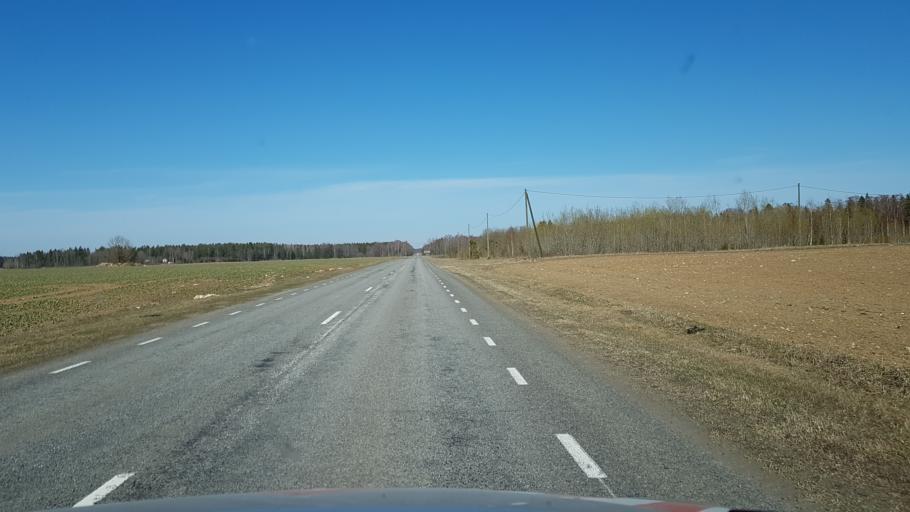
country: EE
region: Laeaene-Virumaa
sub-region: Tamsalu vald
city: Tamsalu
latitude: 59.1317
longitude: 26.0412
